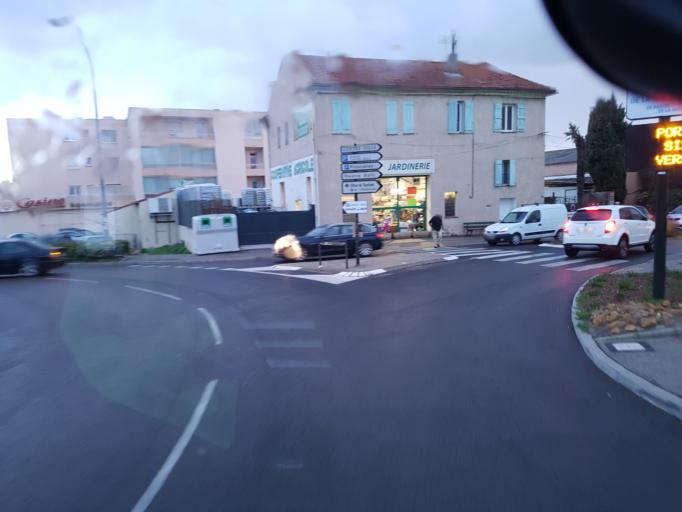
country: FR
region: Provence-Alpes-Cote d'Azur
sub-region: Departement du Var
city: Sanary-sur-Mer
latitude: 43.1215
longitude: 5.8049
